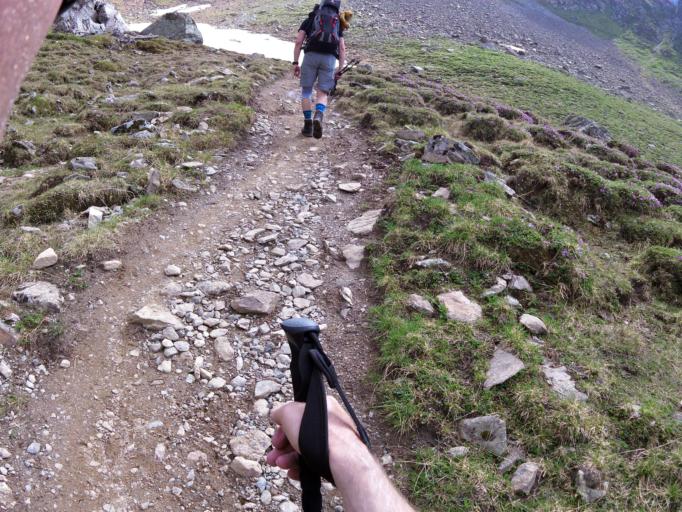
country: AT
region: Tyrol
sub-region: Politischer Bezirk Innsbruck Land
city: Gschnitz
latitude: 47.0475
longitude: 11.3125
